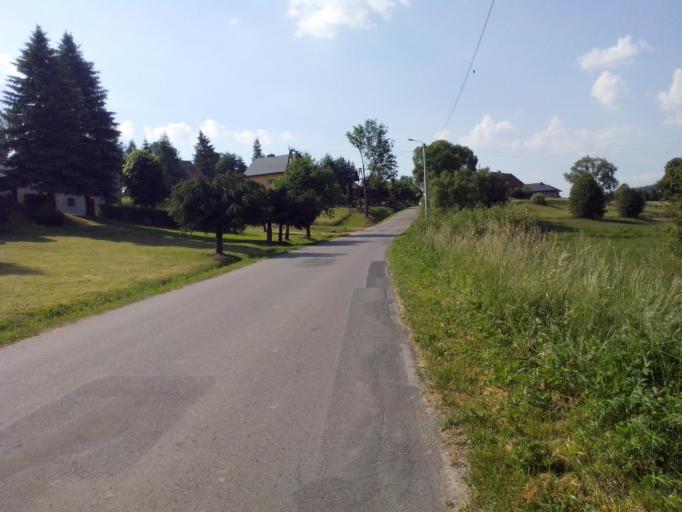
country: PL
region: Subcarpathian Voivodeship
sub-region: Powiat brzozowski
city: Blizne
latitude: 49.7527
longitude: 21.9628
